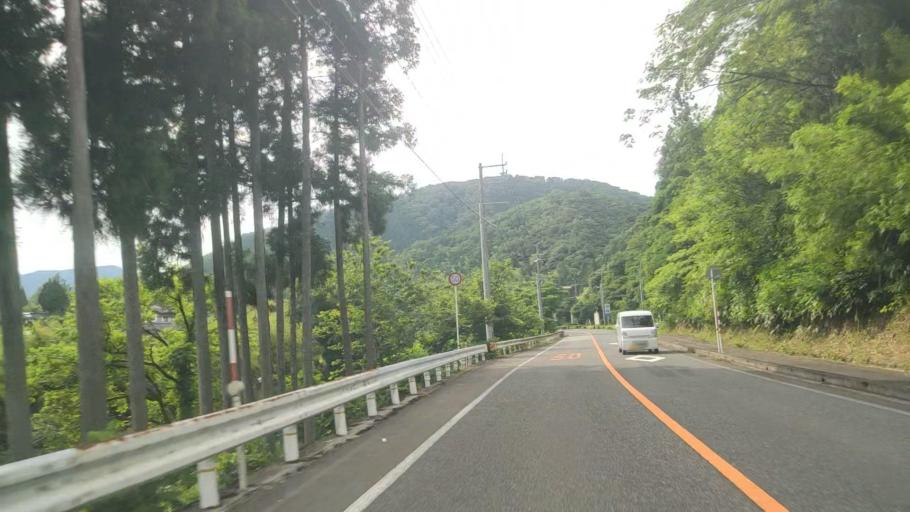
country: JP
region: Tottori
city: Tottori
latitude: 35.3399
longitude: 134.1794
